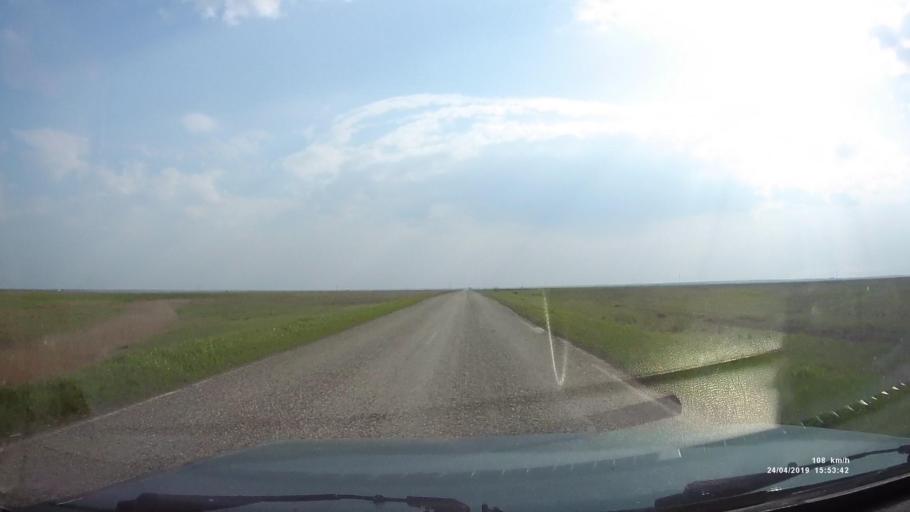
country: RU
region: Kalmykiya
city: Yashalta
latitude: 46.5948
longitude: 42.5722
